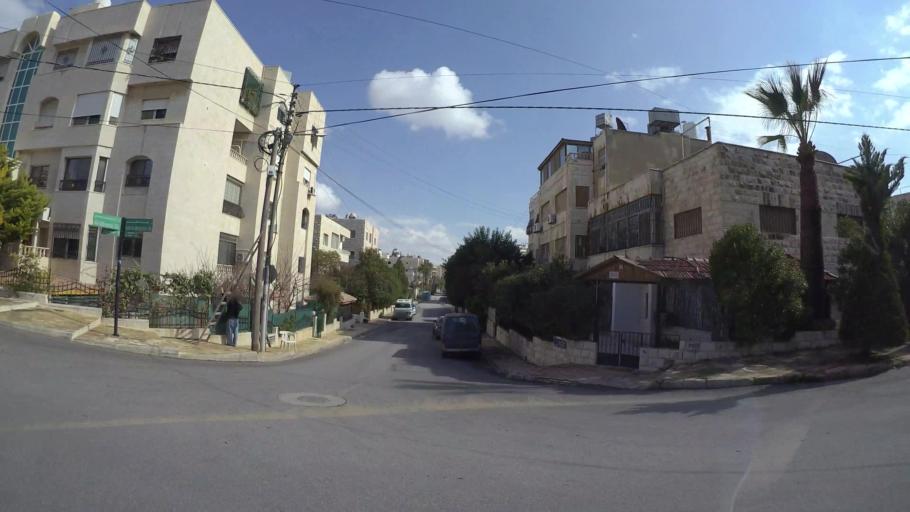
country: JO
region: Amman
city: Al Jubayhah
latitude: 31.9788
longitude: 35.8921
